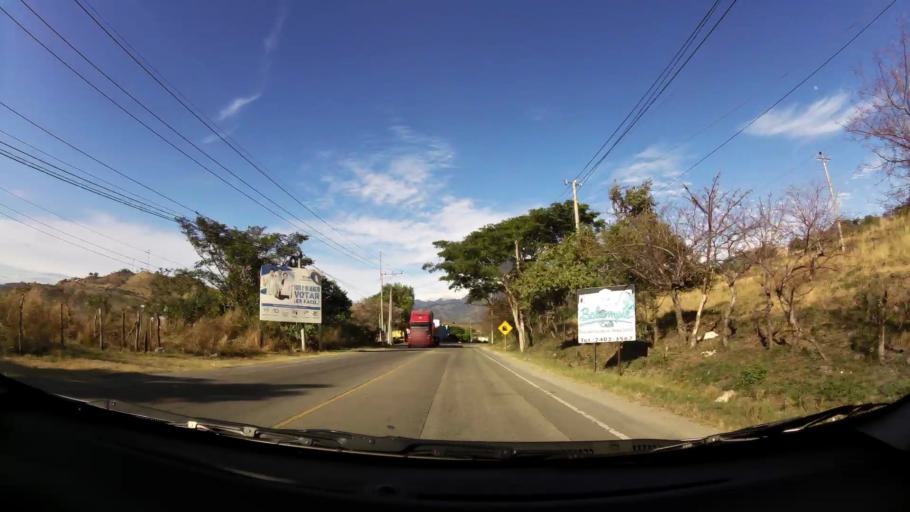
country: SV
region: Santa Ana
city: Metapan
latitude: 14.3097
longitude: -89.4523
